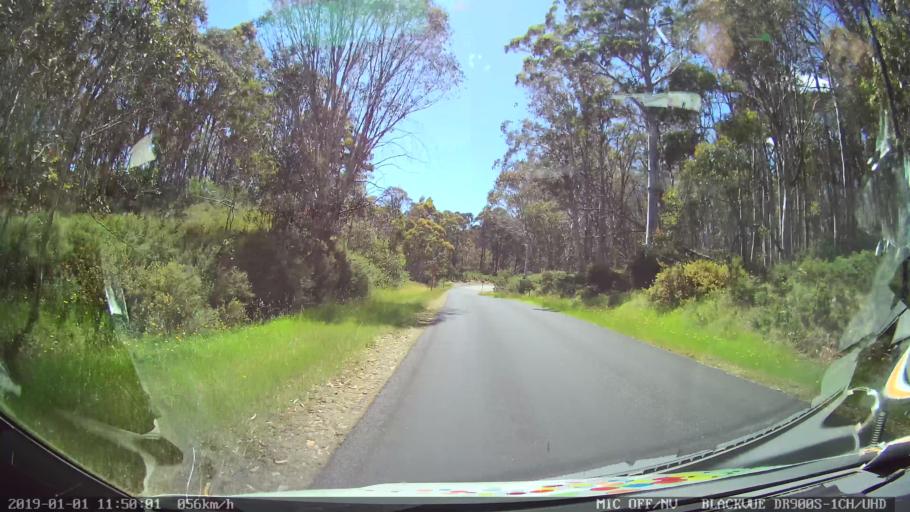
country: AU
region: New South Wales
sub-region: Snowy River
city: Jindabyne
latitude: -35.8909
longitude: 148.4173
